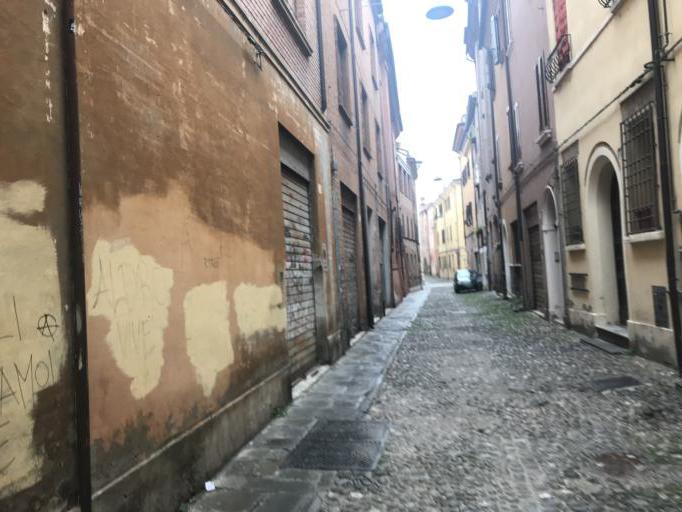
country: IT
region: Emilia-Romagna
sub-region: Provincia di Ferrara
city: Ferrara
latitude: 44.8347
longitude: 11.6220
